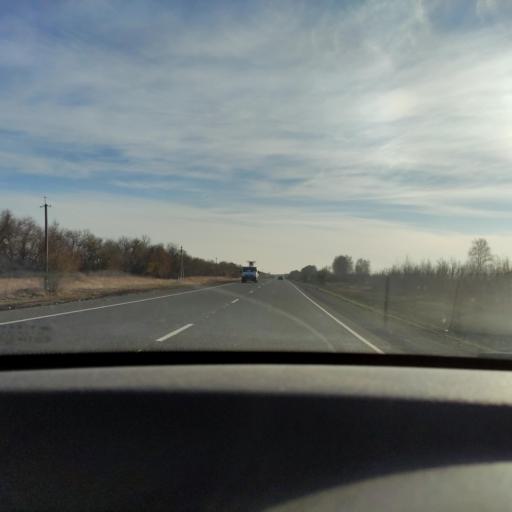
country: RU
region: Samara
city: Krasnoarmeyskoye
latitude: 52.8208
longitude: 50.0093
